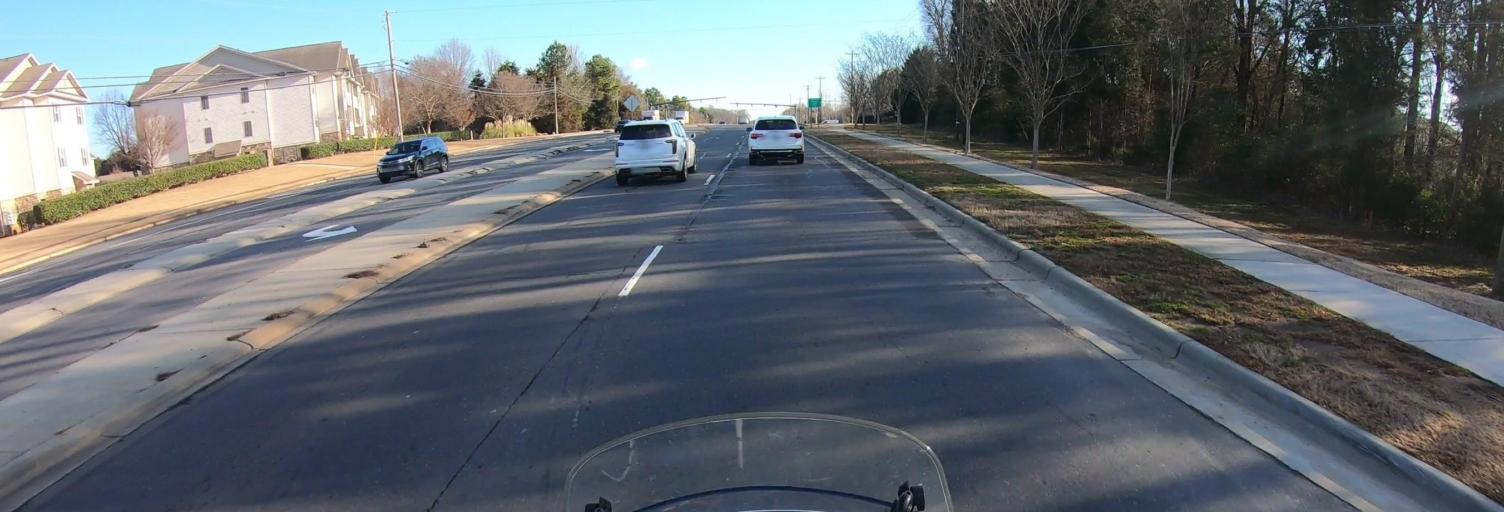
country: US
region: South Carolina
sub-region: York County
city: Lake Wylie
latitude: 35.1067
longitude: -80.9805
